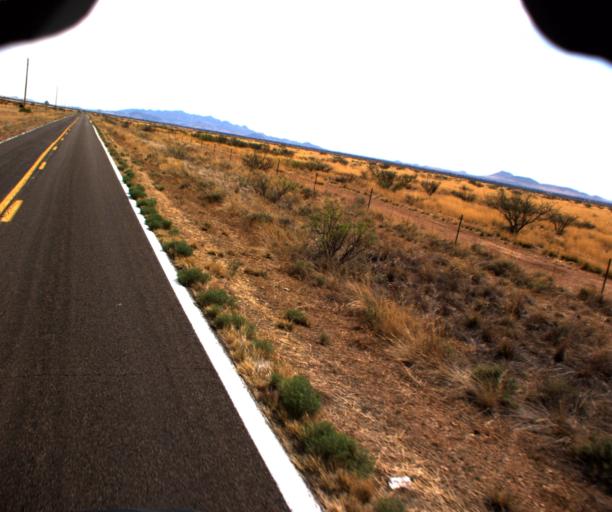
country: US
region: Arizona
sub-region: Cochise County
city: Willcox
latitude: 31.9329
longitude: -109.4914
